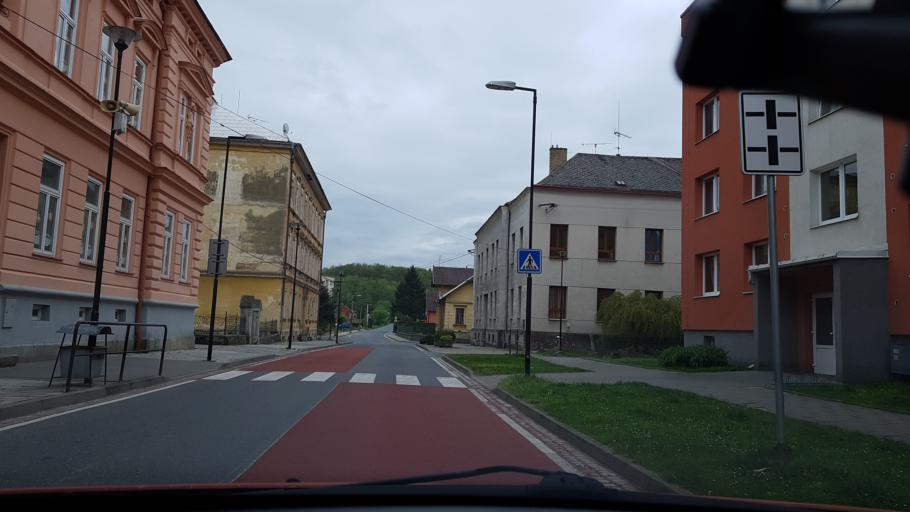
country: CZ
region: Olomoucky
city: Vidnava
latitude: 50.3720
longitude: 17.1870
